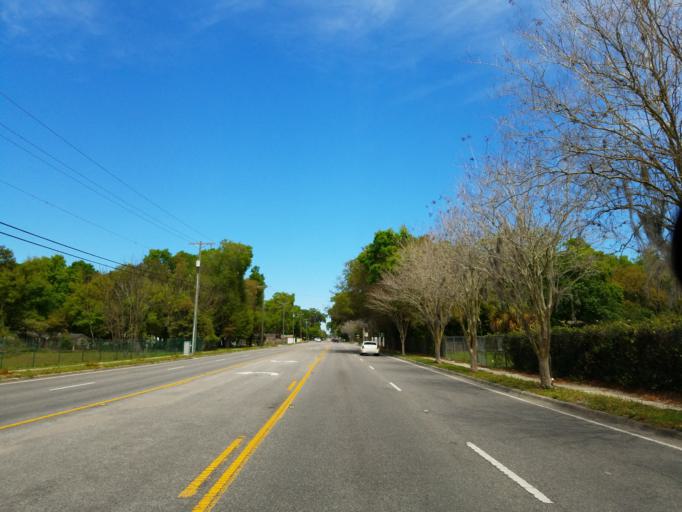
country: US
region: Florida
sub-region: Hillsborough County
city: Seffner
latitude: 27.9671
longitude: -82.2859
